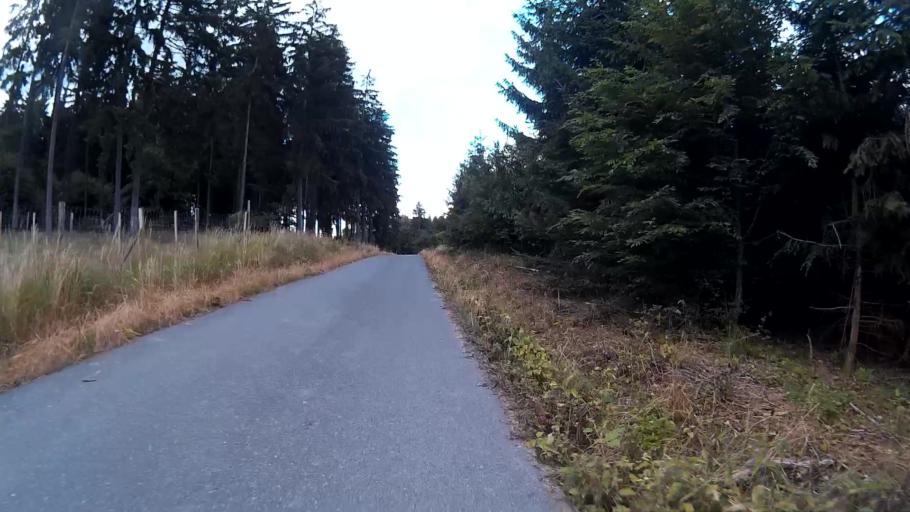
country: CZ
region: South Moravian
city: Veverska Bityska
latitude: 49.2289
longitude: 16.4594
